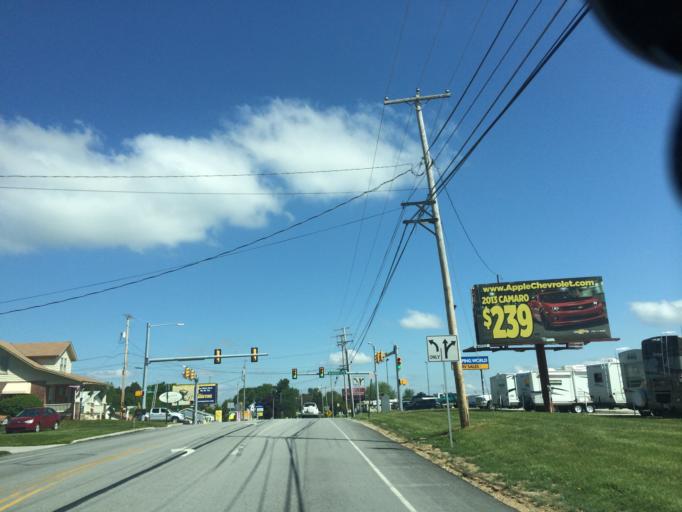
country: US
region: Pennsylvania
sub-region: York County
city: Parkville
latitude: 39.7543
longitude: -76.9529
